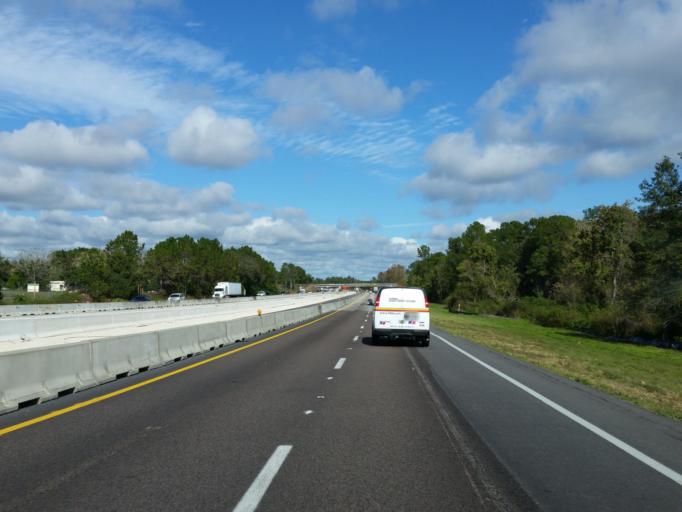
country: US
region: Florida
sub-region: Pasco County
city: Wesley Chapel
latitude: 28.2681
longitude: -82.3290
